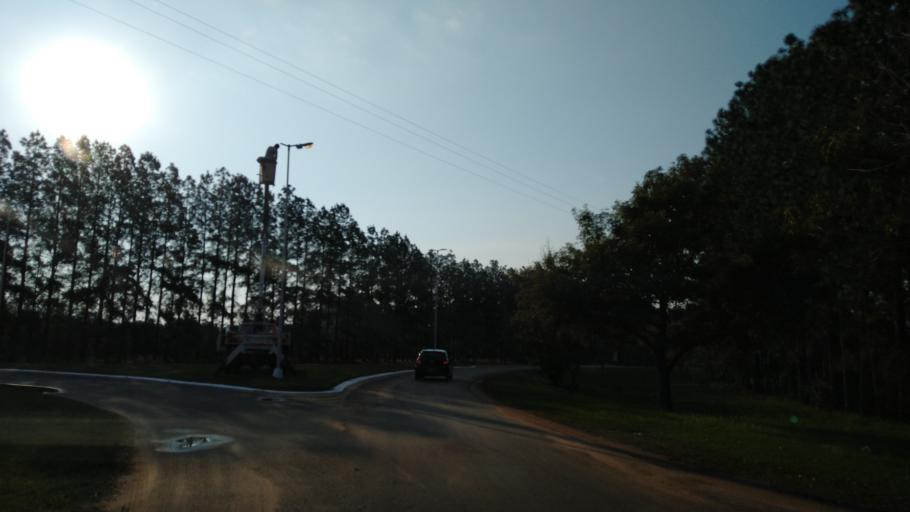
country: AR
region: Entre Rios
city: Santa Ana
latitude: -30.8998
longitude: -57.9238
